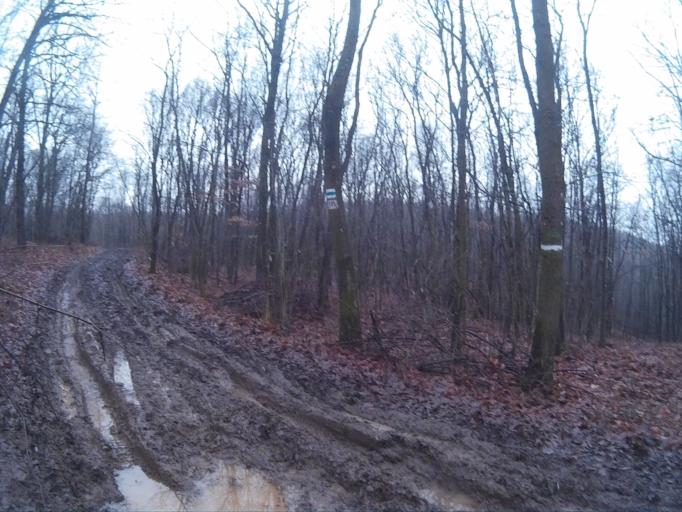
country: HU
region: Komarom-Esztergom
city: Nyergesujfalu
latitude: 47.7066
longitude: 18.5722
